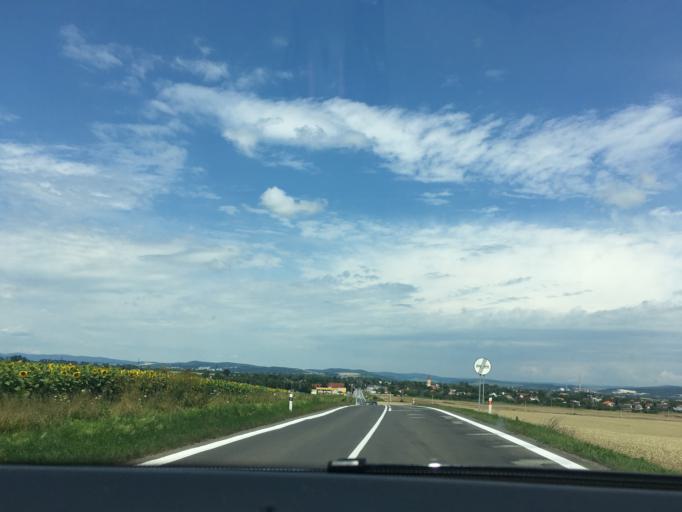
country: SK
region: Presovsky
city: Vranov nad Topl'ou
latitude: 48.8113
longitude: 21.6845
